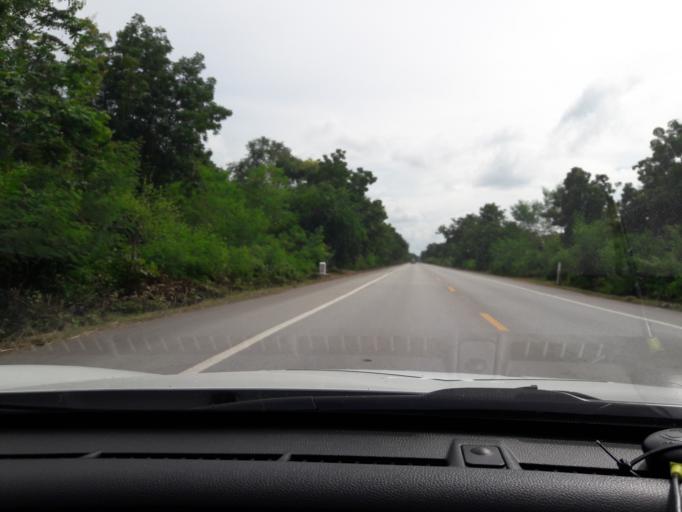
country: TH
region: Nakhon Sawan
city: Tak Fa
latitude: 15.4843
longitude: 100.5364
